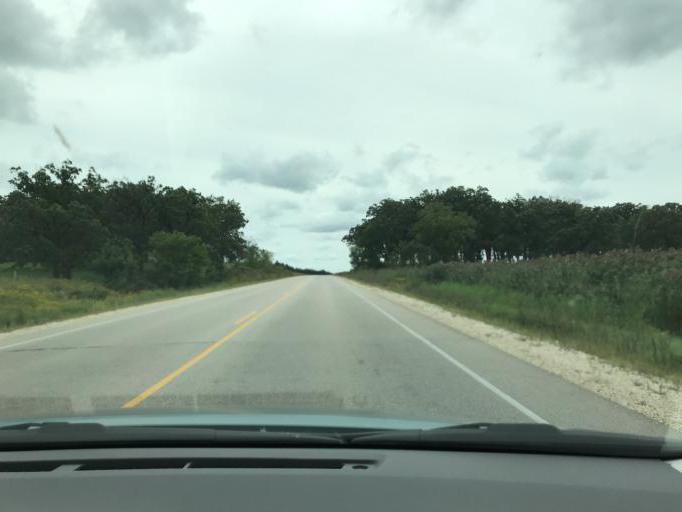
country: US
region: Wisconsin
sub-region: Racine County
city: Bohners Lake
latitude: 42.6068
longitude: -88.2266
